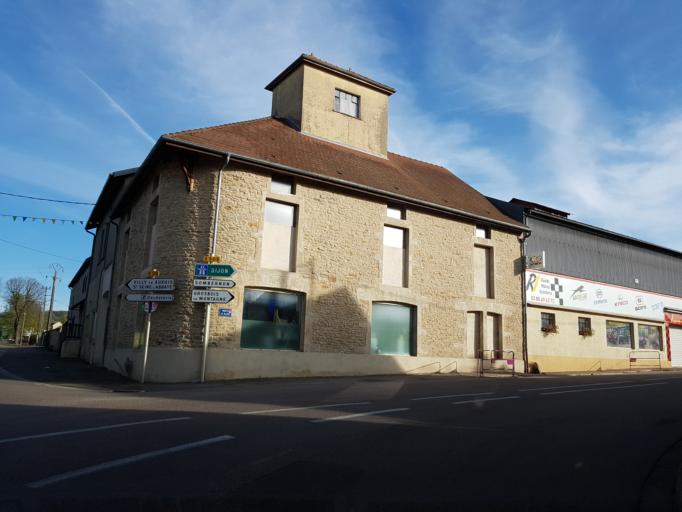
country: FR
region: Bourgogne
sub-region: Departement de la Cote-d'Or
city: Vitteaux
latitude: 47.3959
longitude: 4.5459
